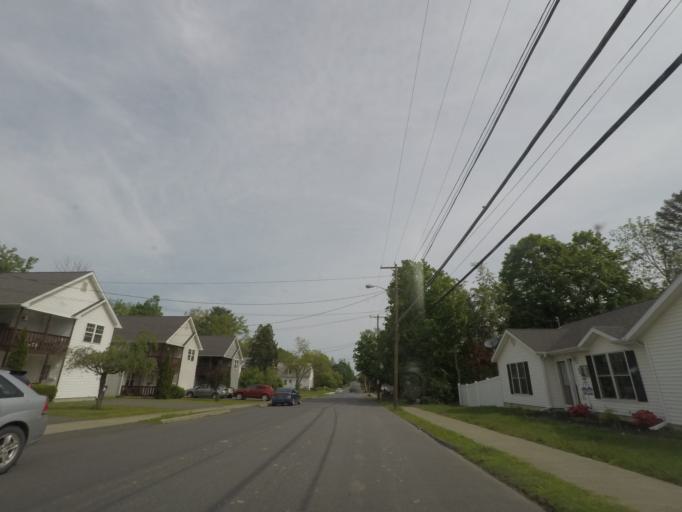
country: US
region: New York
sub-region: Saratoga County
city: Mechanicville
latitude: 42.8896
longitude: -73.6882
